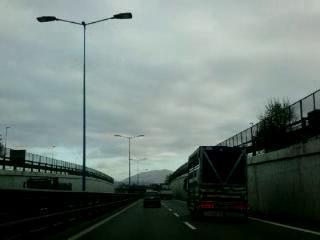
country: IT
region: Lombardy
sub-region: Provincia di Brescia
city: Roncadelle
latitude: 45.5299
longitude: 10.1773
